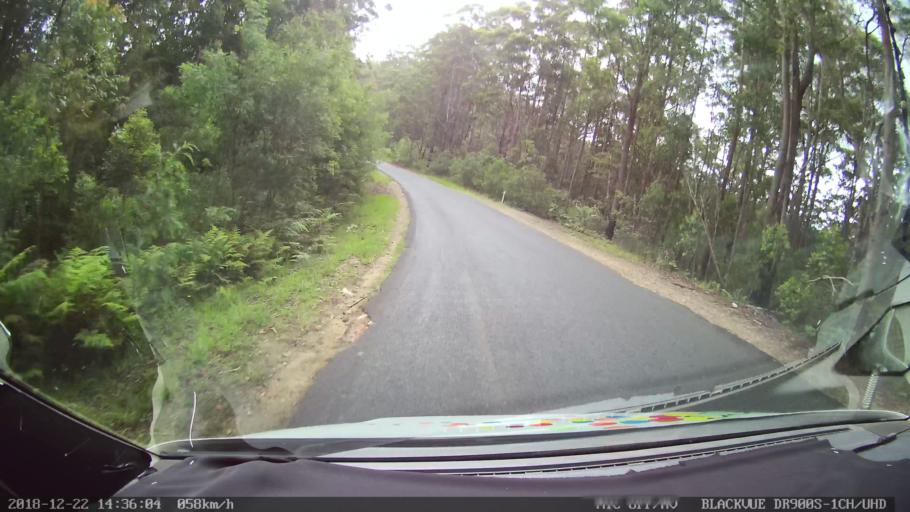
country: AU
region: New South Wales
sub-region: Bellingen
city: Dorrigo
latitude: -30.1260
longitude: 152.6087
